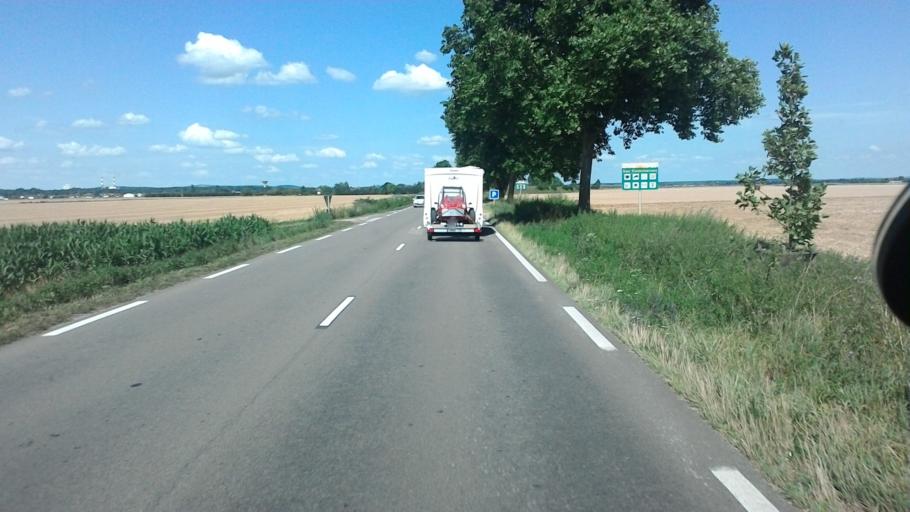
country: FR
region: Franche-Comte
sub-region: Departement du Jura
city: Tavaux
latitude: 47.0243
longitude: 5.3896
